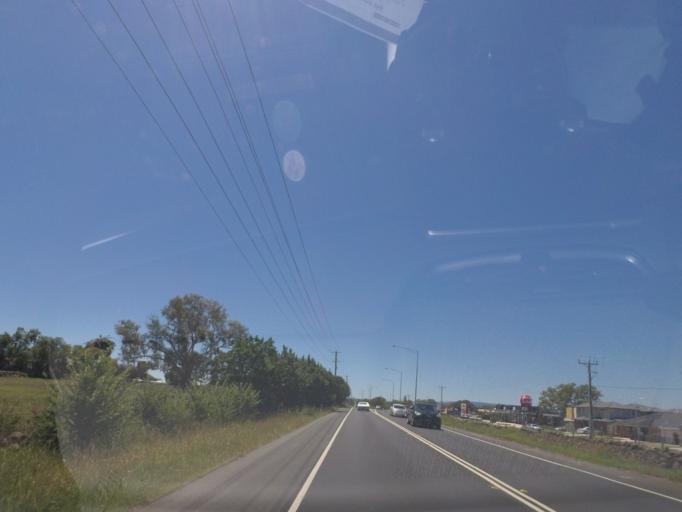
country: AU
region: Victoria
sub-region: Whittlesea
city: Epping
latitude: -37.6181
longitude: 145.0297
